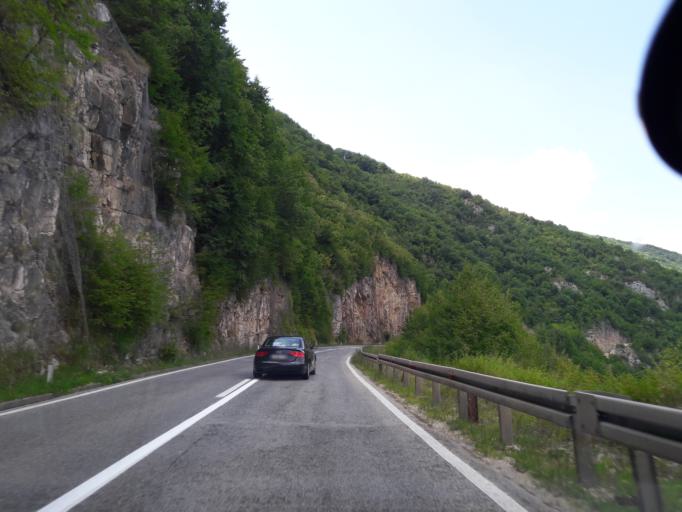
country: BA
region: Republika Srpska
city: Mrkonjic Grad
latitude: 44.4926
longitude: 17.1540
